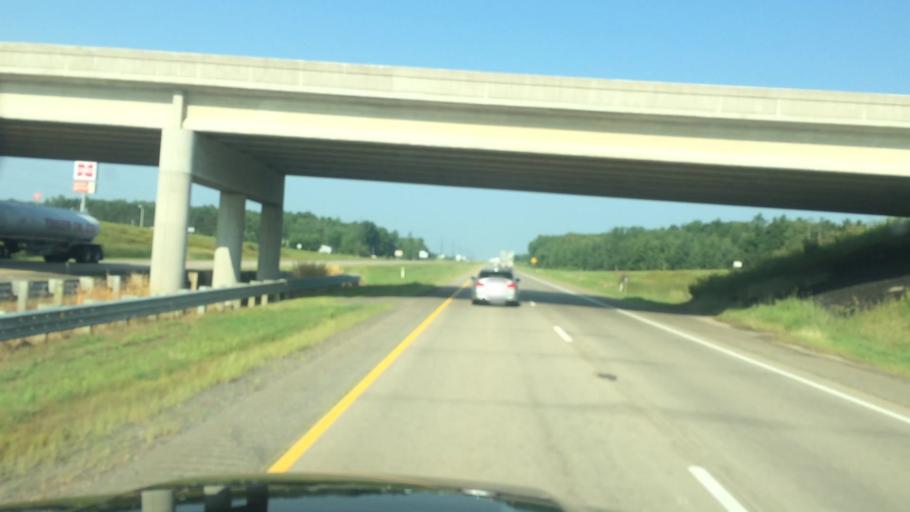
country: US
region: Wisconsin
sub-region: Marathon County
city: Edgar
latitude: 44.9445
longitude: -89.9633
